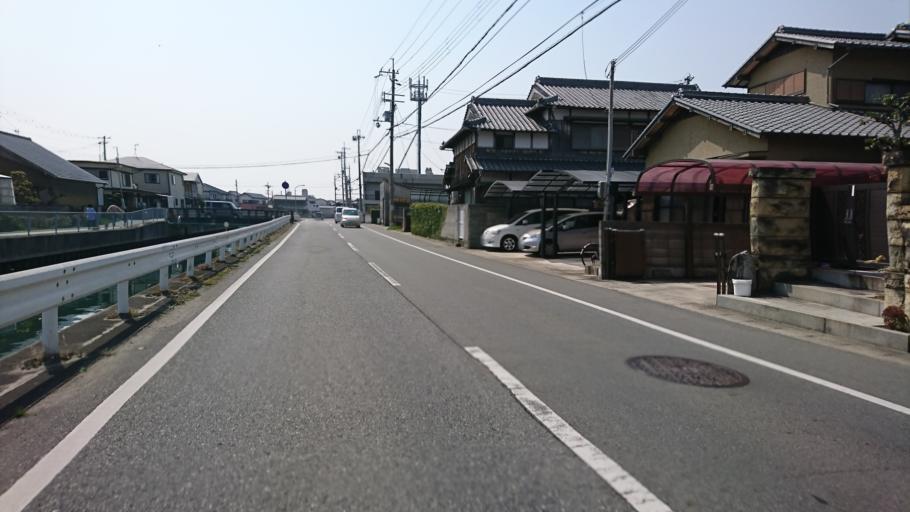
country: JP
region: Hyogo
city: Shirahamacho-usazakiminami
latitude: 34.7841
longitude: 134.7514
